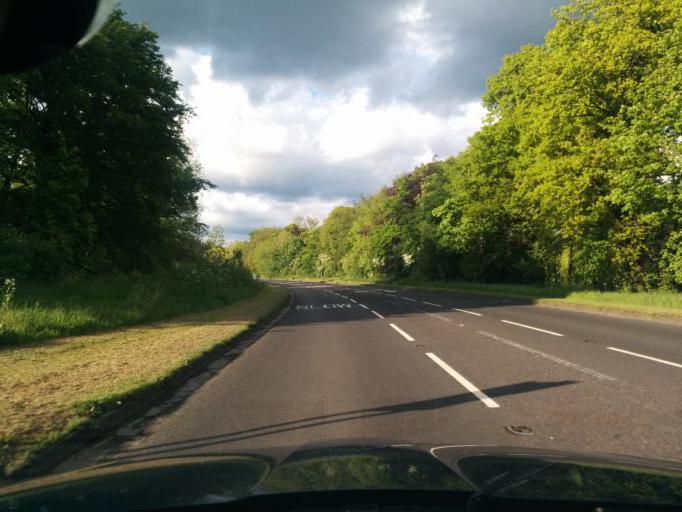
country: GB
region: England
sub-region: Northumberland
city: Bedlington
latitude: 55.1176
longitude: -1.6175
